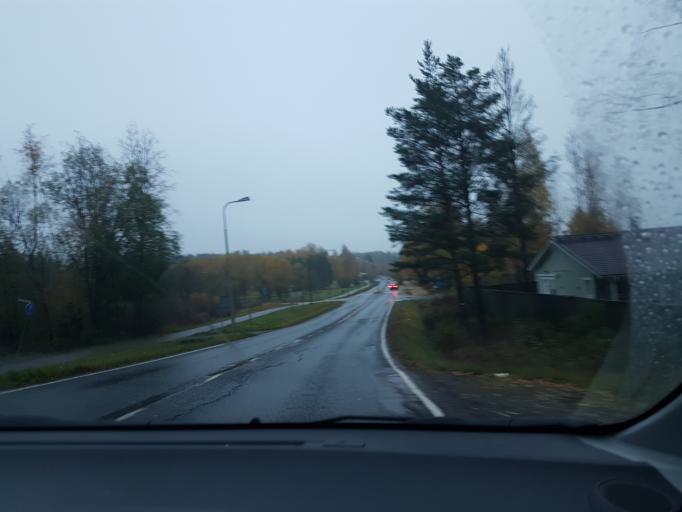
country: FI
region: Uusimaa
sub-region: Helsinki
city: Jaervenpaeae
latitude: 60.5374
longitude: 25.1124
